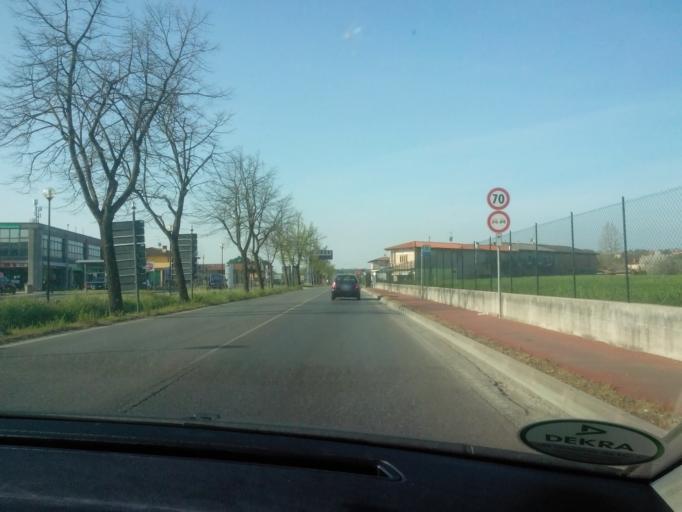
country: IT
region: Lombardy
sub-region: Provincia di Brescia
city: Manerba del Garda
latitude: 45.5471
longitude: 10.5333
